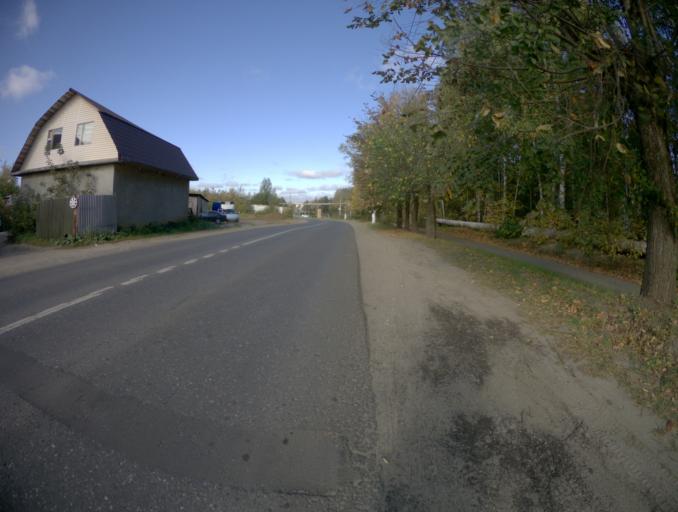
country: RU
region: Moskovskaya
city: Roshal'
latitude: 55.6619
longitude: 39.8720
